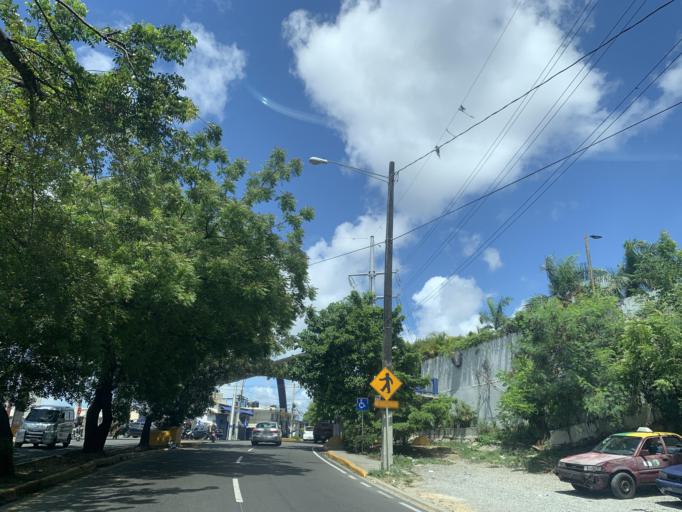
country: DO
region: Nacional
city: La Agustina
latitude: 18.5059
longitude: -69.9220
